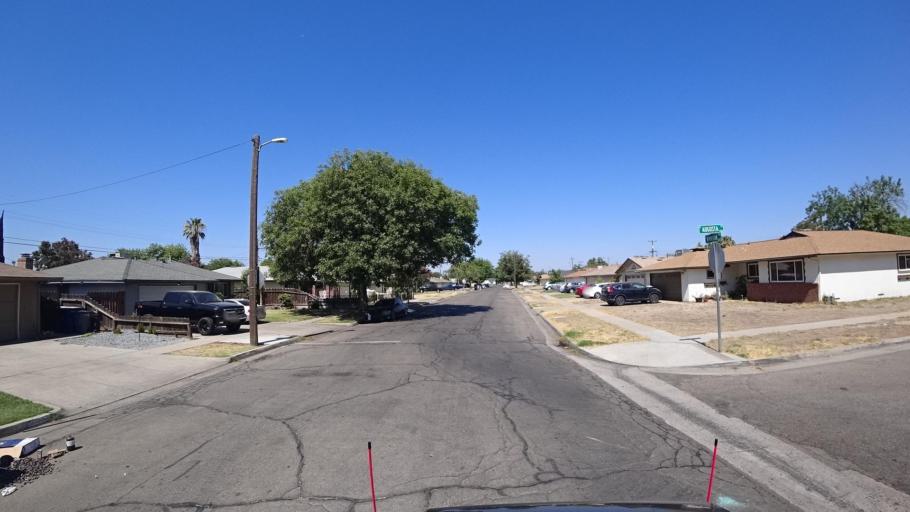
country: US
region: California
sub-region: Fresno County
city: Fresno
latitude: 36.7919
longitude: -119.7791
